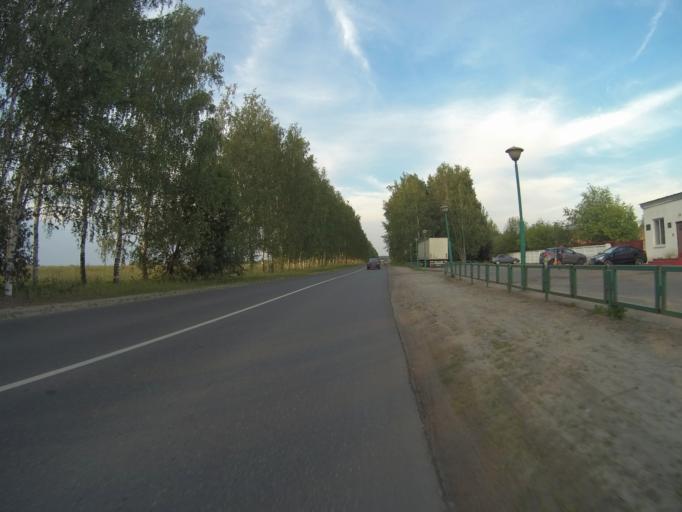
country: RU
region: Vladimir
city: Raduzhnyy
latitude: 56.0064
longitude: 40.2995
